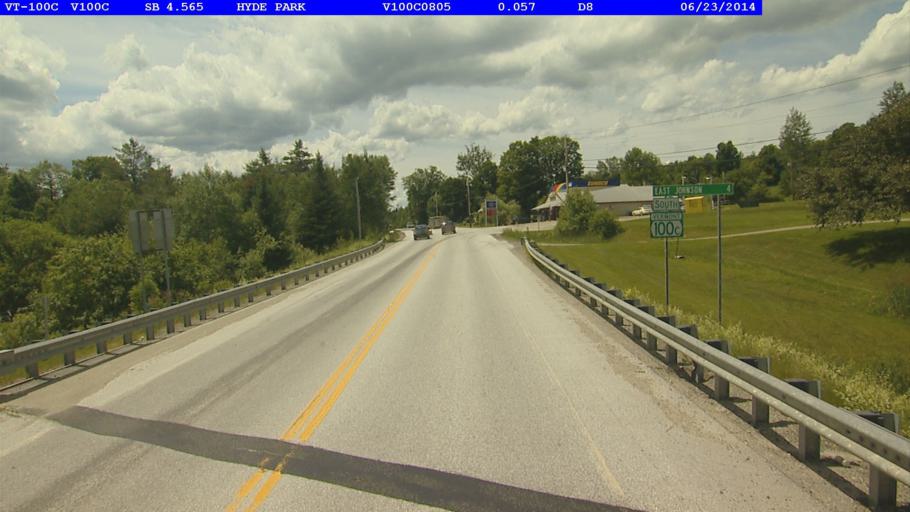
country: US
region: Vermont
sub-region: Lamoille County
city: Hyde Park
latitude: 44.6665
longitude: -72.6053
